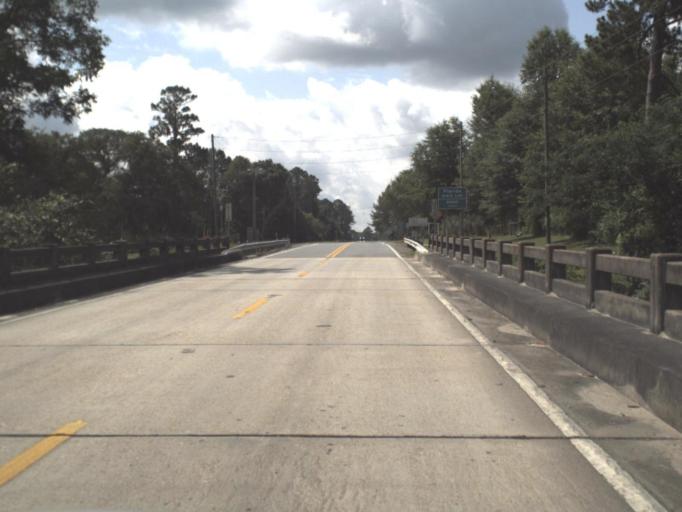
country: US
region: Florida
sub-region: Baker County
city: Macclenny
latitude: 30.3623
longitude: -82.1344
